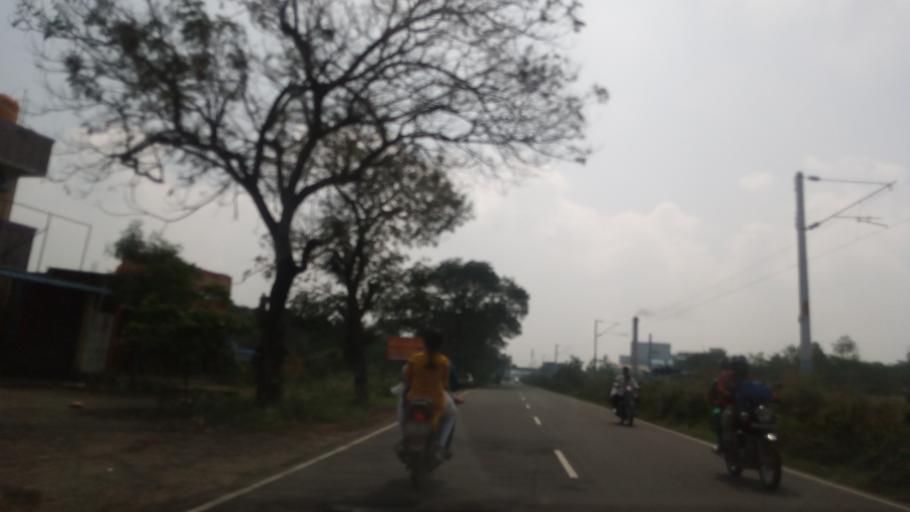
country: IN
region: Tamil Nadu
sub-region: Kancheepuram
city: Kanchipuram
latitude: 12.8803
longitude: 79.6892
